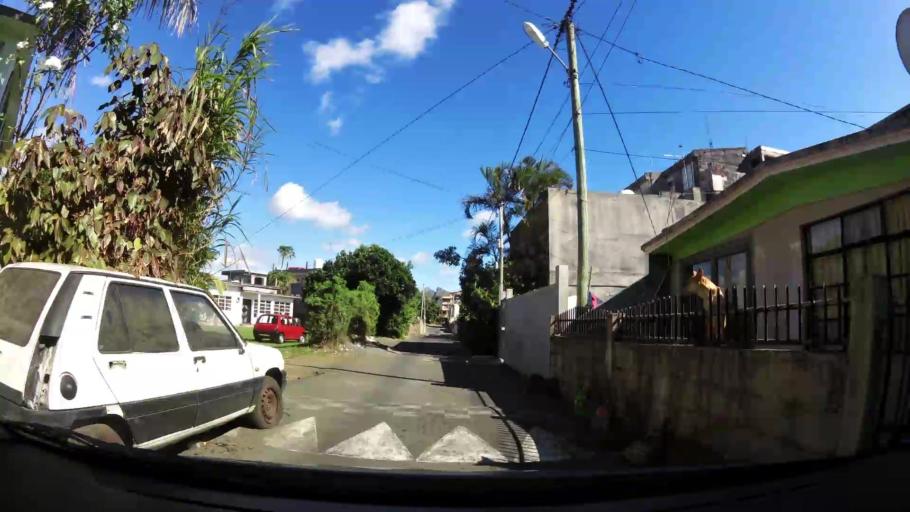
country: MU
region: Plaines Wilhems
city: Quatre Bornes
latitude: -20.2796
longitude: 57.4739
